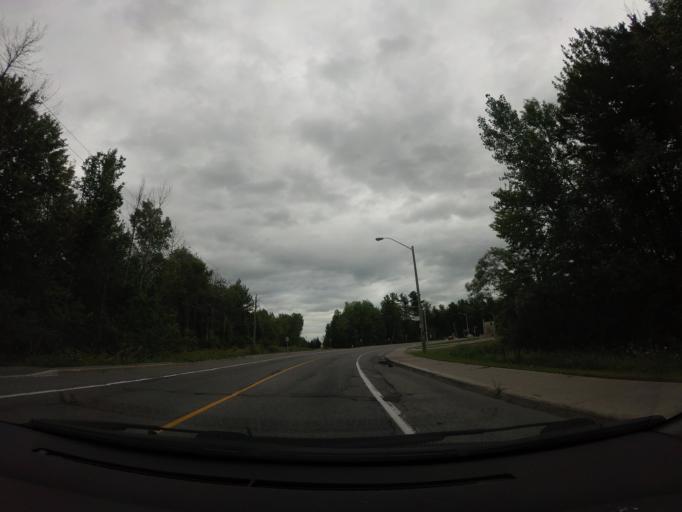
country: CA
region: Ontario
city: Ottawa
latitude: 45.4400
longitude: -75.5436
